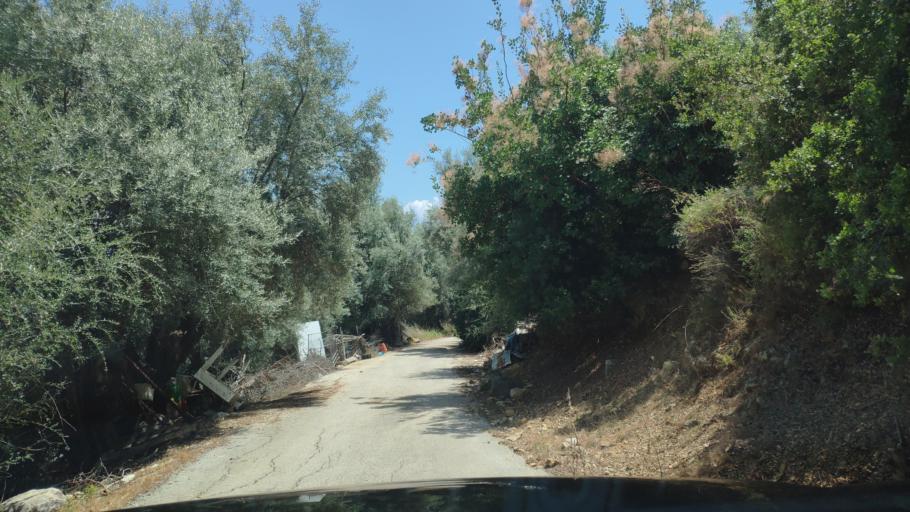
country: GR
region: Ionian Islands
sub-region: Lefkada
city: Nidri
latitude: 38.7539
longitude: 20.7133
